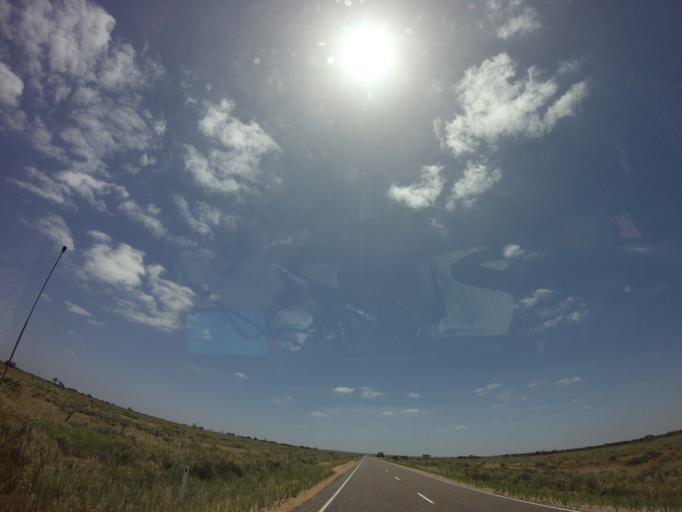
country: AU
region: South Australia
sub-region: Whyalla
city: Whyalla
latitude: -32.8595
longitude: 137.0078
